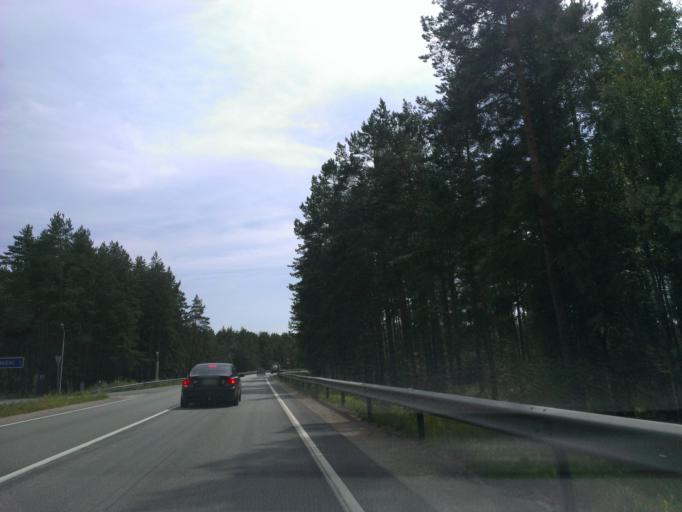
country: LV
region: Riga
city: Bergi
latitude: 56.9601
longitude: 24.3749
